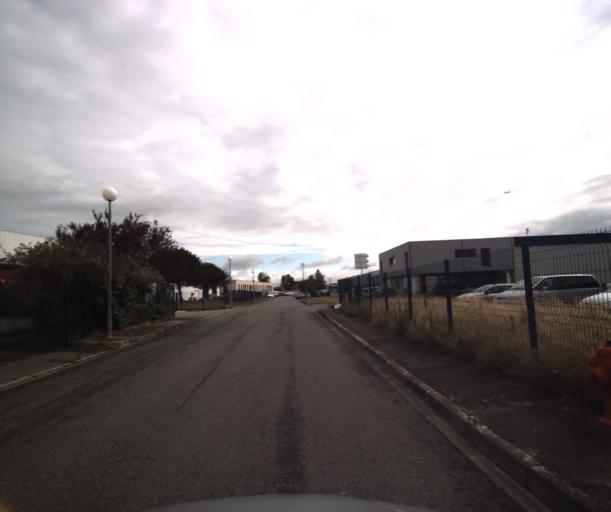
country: FR
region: Midi-Pyrenees
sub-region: Departement de la Haute-Garonne
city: Portet-sur-Garonne
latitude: 43.5455
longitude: 1.4133
